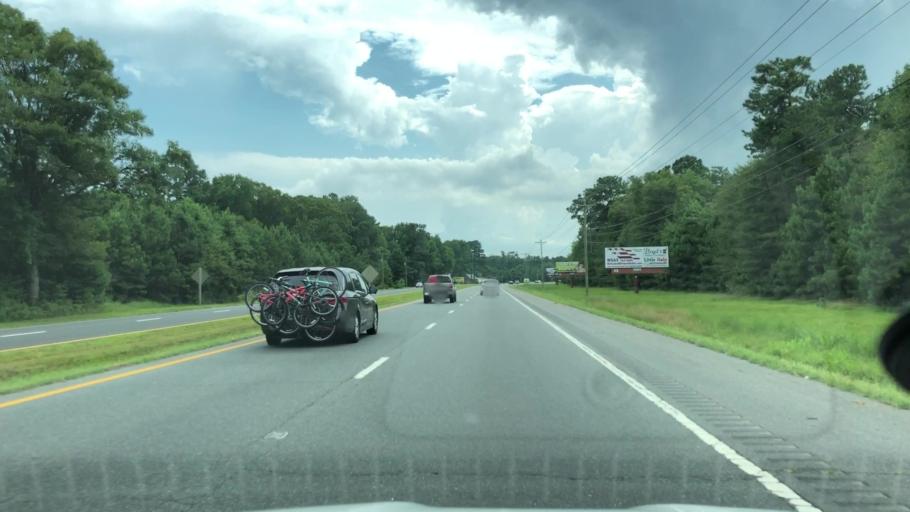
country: US
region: Virginia
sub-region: Accomack County
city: Wattsville
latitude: 37.8314
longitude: -75.5784
